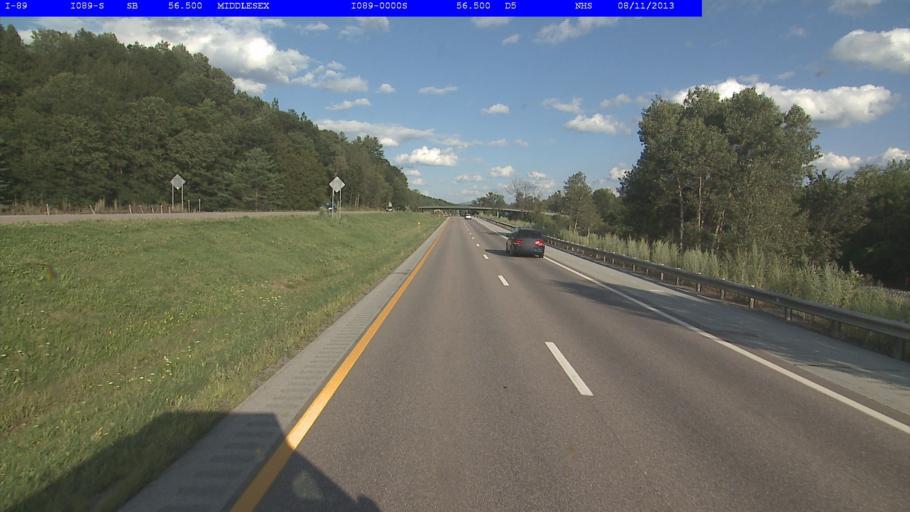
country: US
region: Vermont
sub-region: Washington County
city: Montpelier
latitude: 44.2774
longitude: -72.6535
